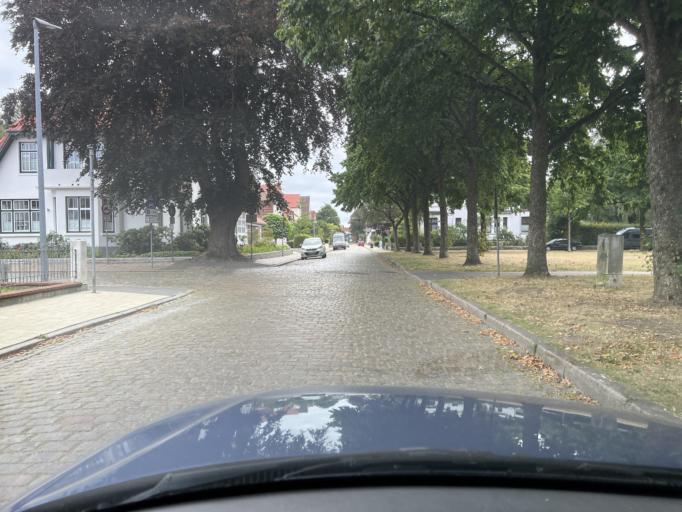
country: DE
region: Schleswig-Holstein
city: Heide
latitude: 54.1900
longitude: 9.0941
